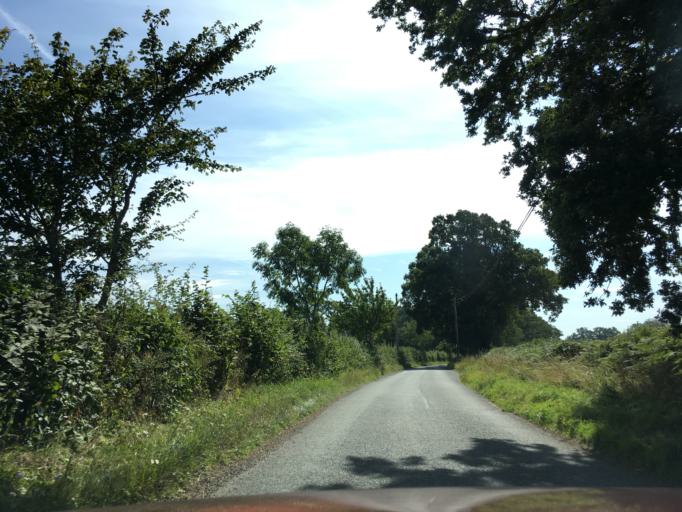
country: GB
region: England
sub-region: West Berkshire
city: Kintbury
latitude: 51.3718
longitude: -1.4358
